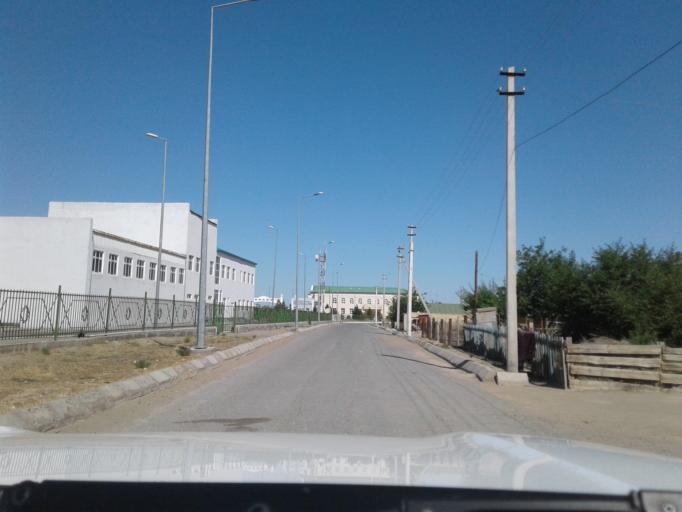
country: TM
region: Mary
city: Bayramaly
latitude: 38.0884
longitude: 62.7977
